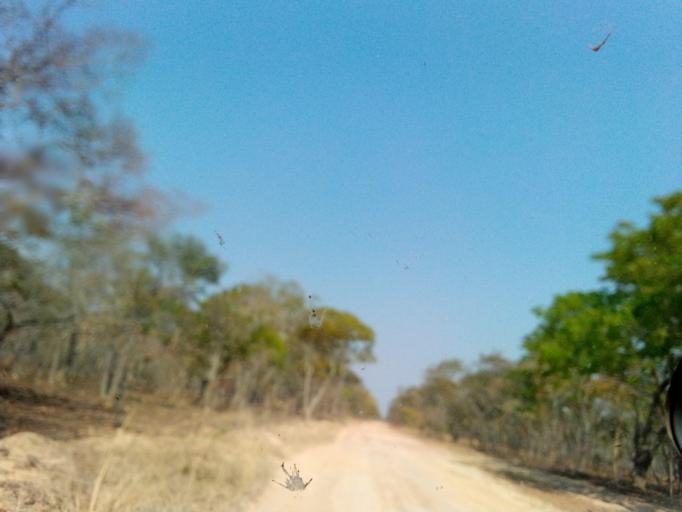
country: ZM
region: Northern
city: Mpika
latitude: -12.2422
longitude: 30.8365
